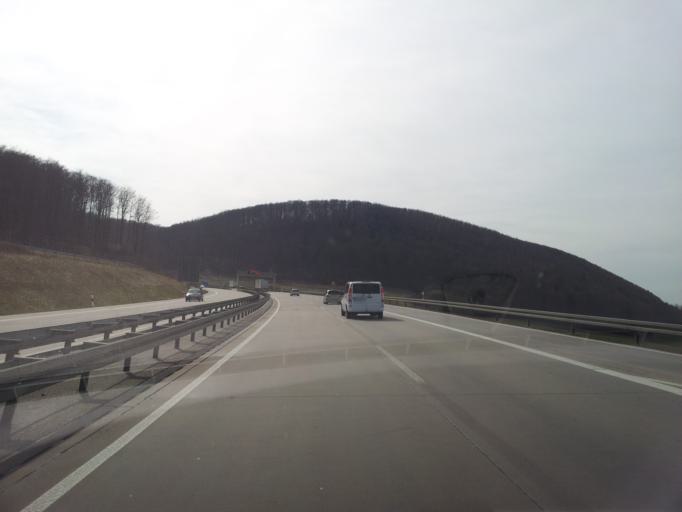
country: DE
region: Thuringia
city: Einhausen
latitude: 50.5210
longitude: 10.4620
